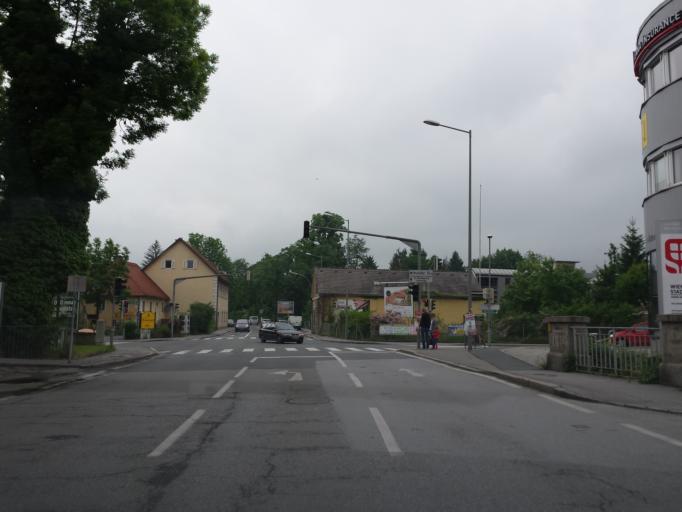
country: AT
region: Styria
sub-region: Graz Stadt
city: Goesting
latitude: 47.1013
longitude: 15.4257
